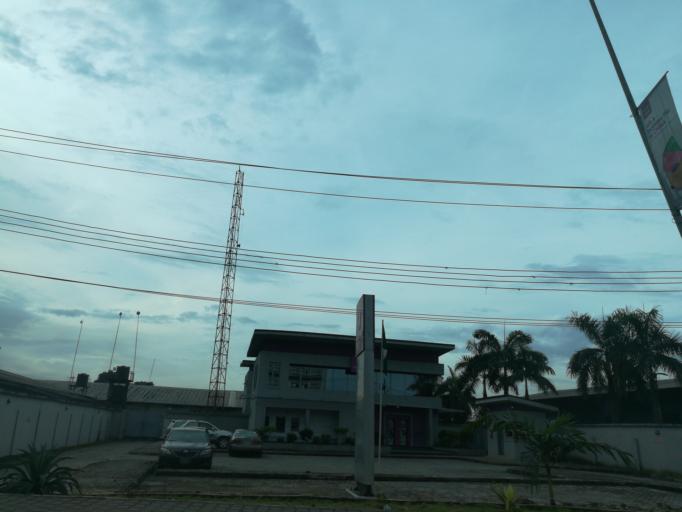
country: NG
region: Rivers
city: Port Harcourt
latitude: 4.8093
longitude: 7.0143
